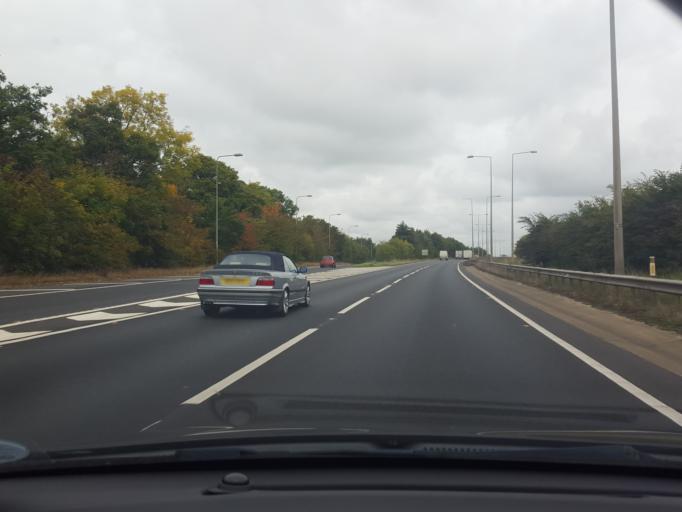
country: GB
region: England
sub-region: Suffolk
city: Capel Saint Mary
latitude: 52.0120
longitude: 1.0658
